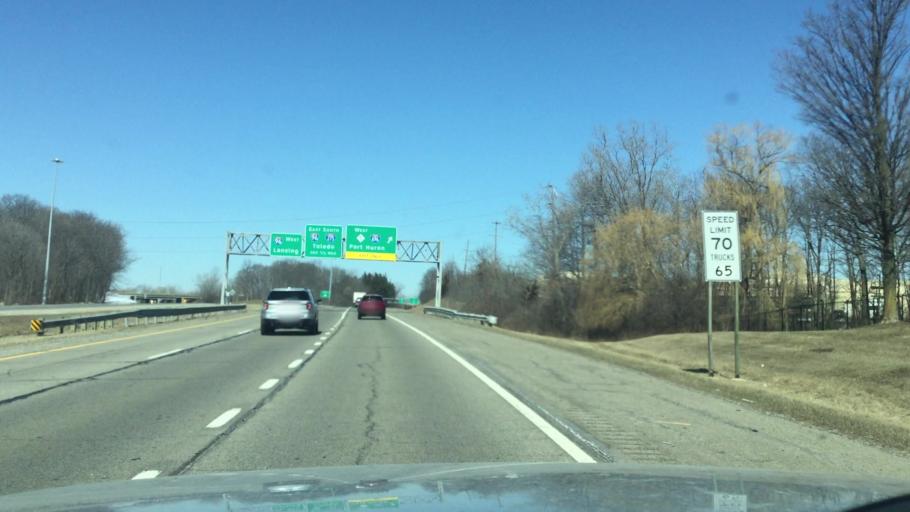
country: US
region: Michigan
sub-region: Oakland County
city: Farmington Hills
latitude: 42.4746
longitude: -83.4215
